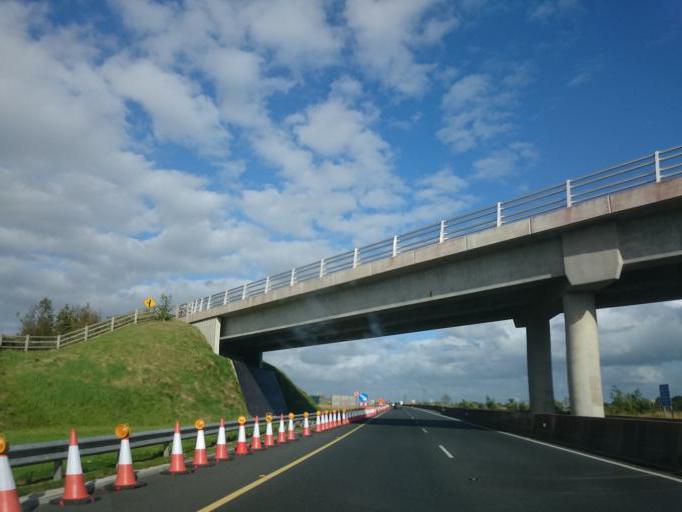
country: IE
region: Connaught
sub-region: County Galway
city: Athenry
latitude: 53.2983
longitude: -8.8267
